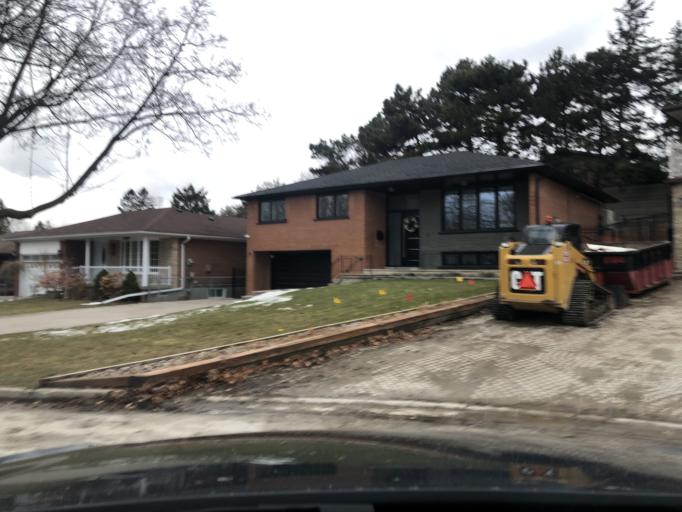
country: CA
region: Ontario
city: Etobicoke
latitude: 43.6934
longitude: -79.5298
